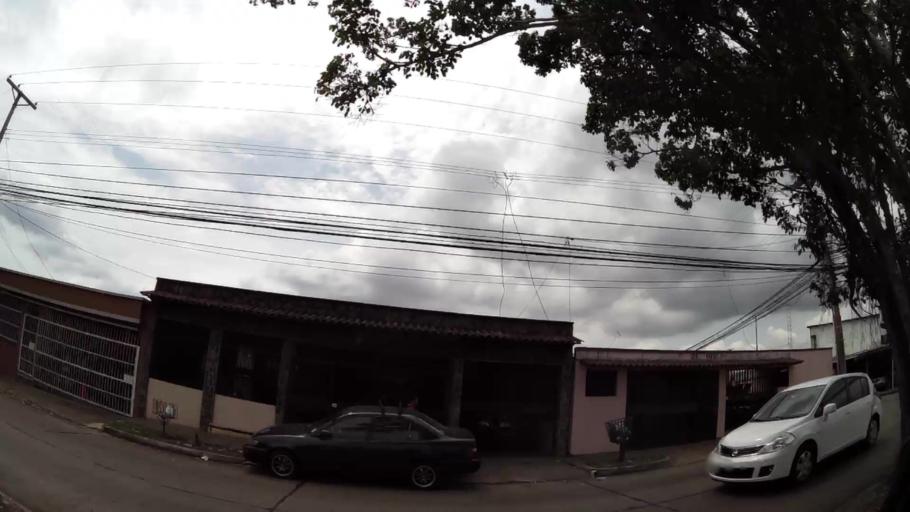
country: PA
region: Panama
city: San Miguelito
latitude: 9.0532
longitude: -79.4221
